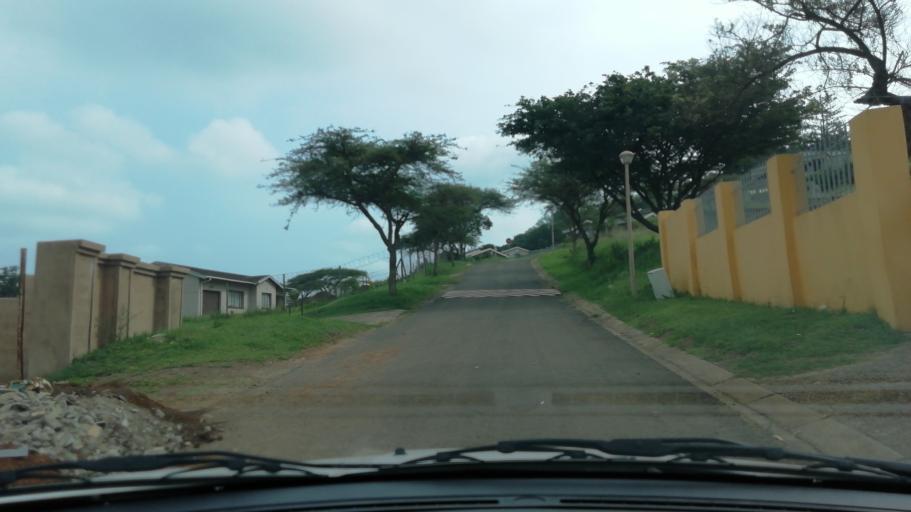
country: ZA
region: KwaZulu-Natal
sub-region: uThungulu District Municipality
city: Empangeni
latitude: -28.7394
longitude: 31.8809
